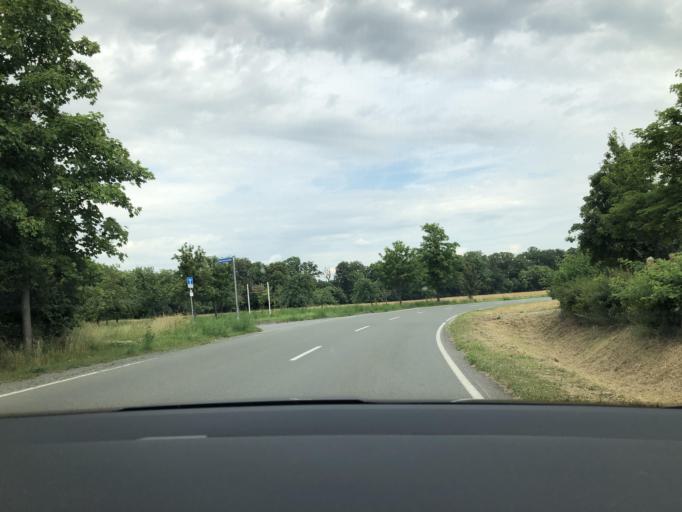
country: DE
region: Saxony-Anhalt
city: Blankenburg
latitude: 51.8084
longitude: 10.9282
